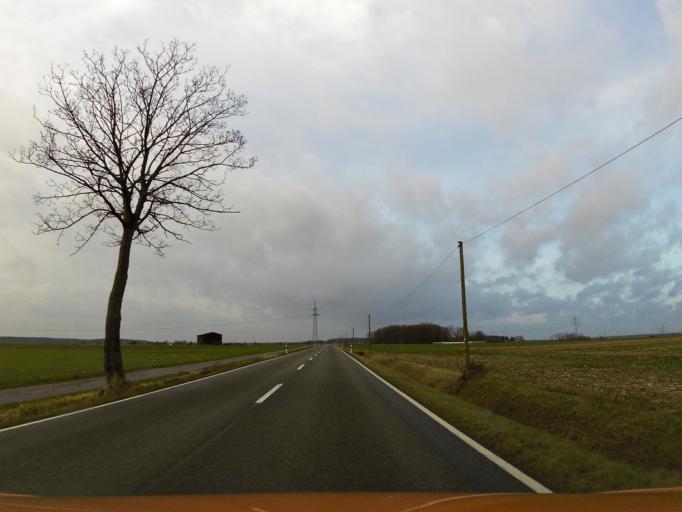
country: DE
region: Lower Saxony
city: Gross Twulpstedt
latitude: 52.3519
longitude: 10.9396
